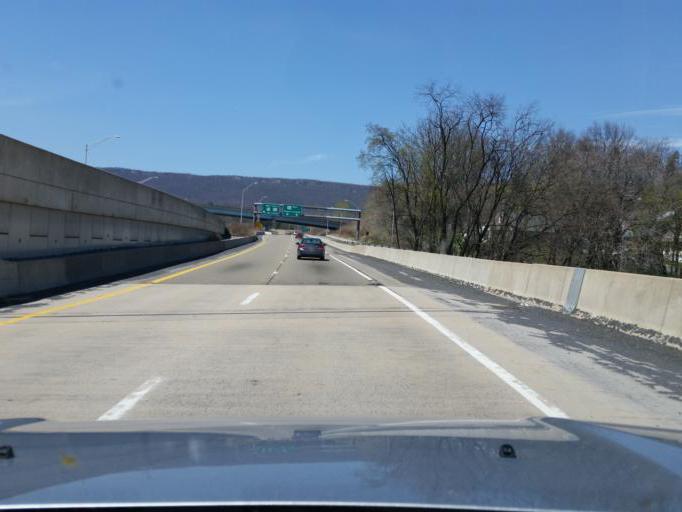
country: US
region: Pennsylvania
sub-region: Mifflin County
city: Highland Park
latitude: 40.6134
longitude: -77.5701
